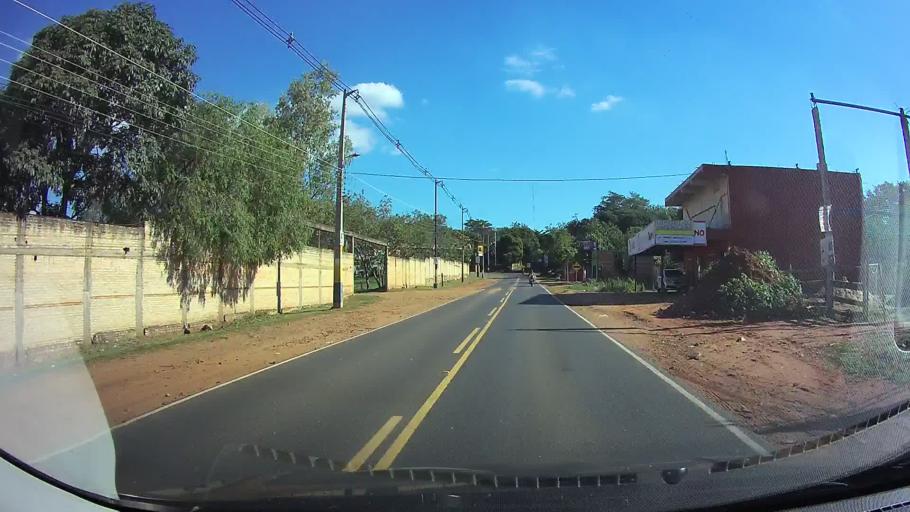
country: PY
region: Central
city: Limpio
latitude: -25.2197
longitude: -57.4774
